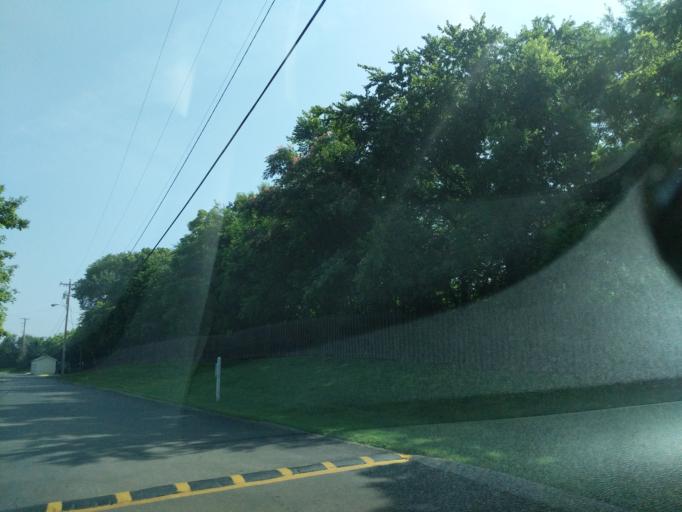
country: US
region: Tennessee
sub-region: Davidson County
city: Goodlettsville
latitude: 36.2980
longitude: -86.7075
